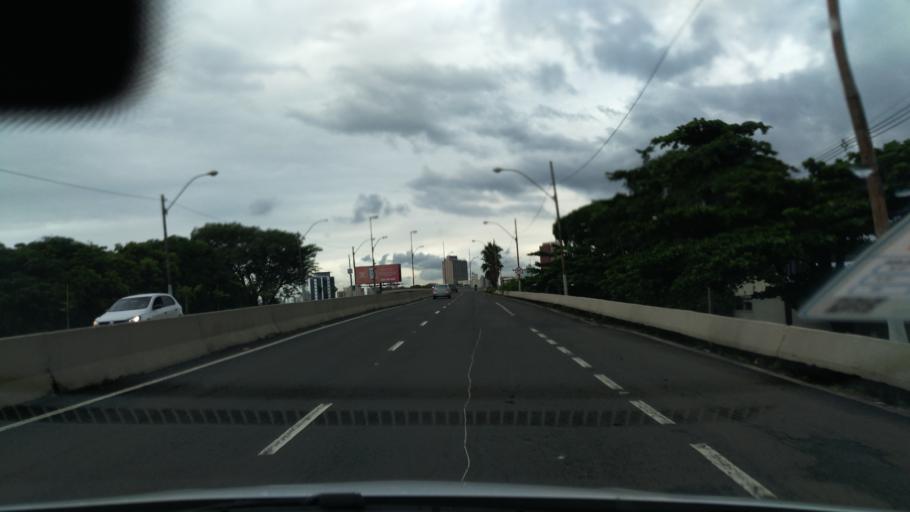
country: BR
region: Sao Paulo
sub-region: Campinas
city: Campinas
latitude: -22.9036
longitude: -47.0754
